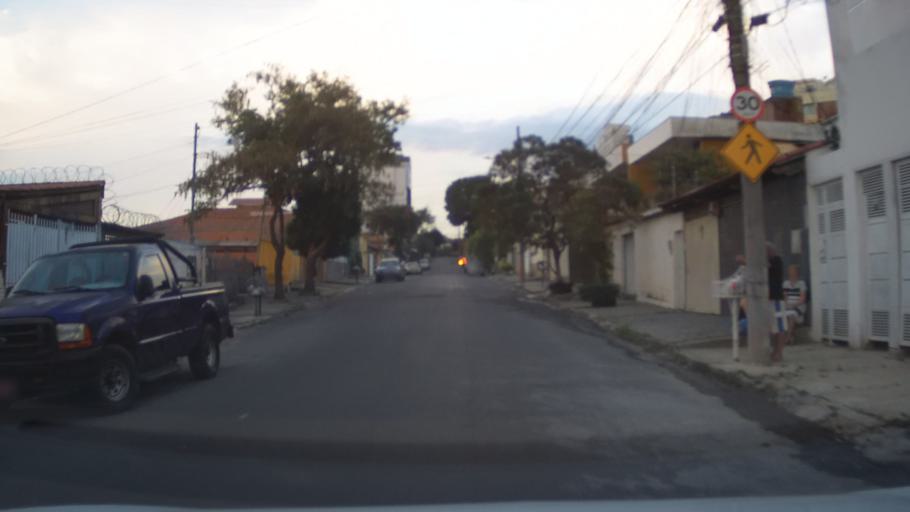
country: BR
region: Minas Gerais
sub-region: Belo Horizonte
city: Belo Horizonte
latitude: -19.8904
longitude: -43.9344
